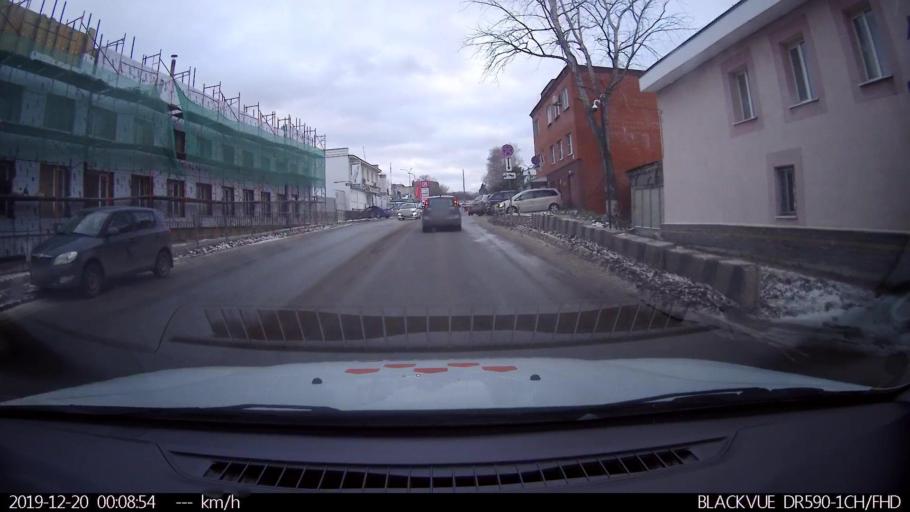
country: RU
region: Jaroslavl
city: Yaroslavl
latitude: 57.7269
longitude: 39.7456
